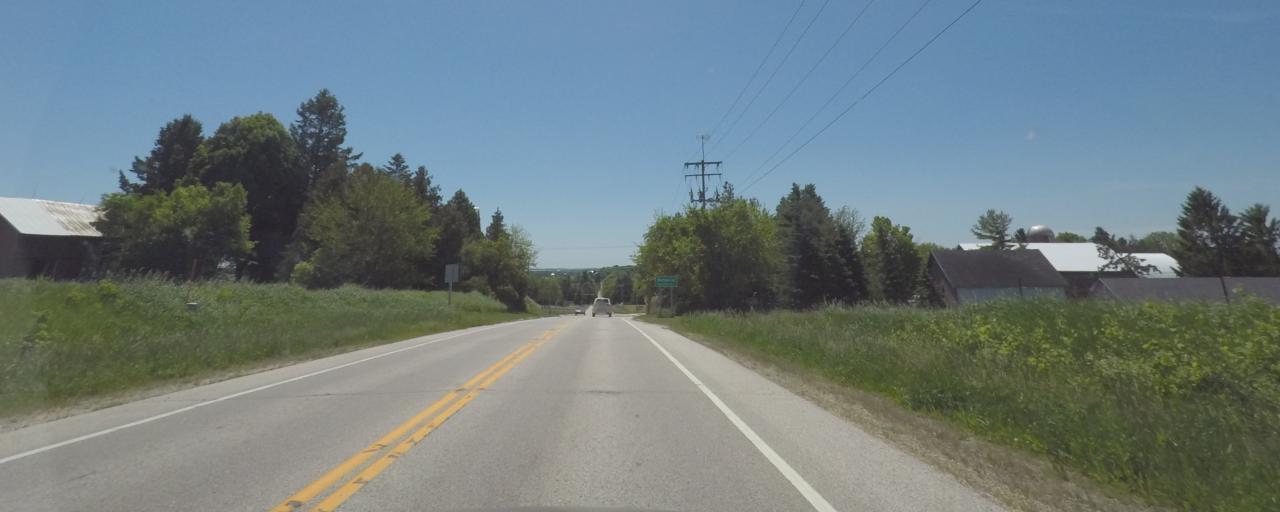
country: US
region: Wisconsin
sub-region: Sheboygan County
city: Random Lake
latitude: 43.6017
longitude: -88.0503
